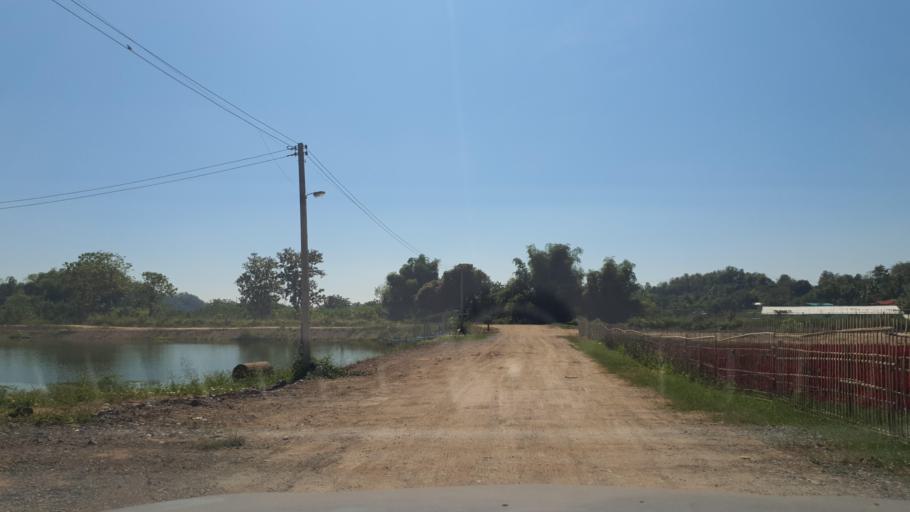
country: TH
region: Chiang Mai
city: Mae Wang
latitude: 18.6840
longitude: 98.8108
